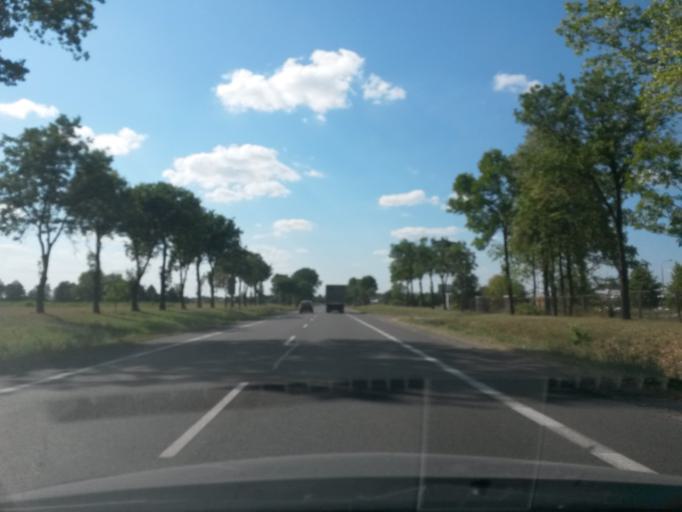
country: PL
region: Masovian Voivodeship
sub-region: Powiat plonski
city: Plonsk
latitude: 52.6141
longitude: 20.3520
